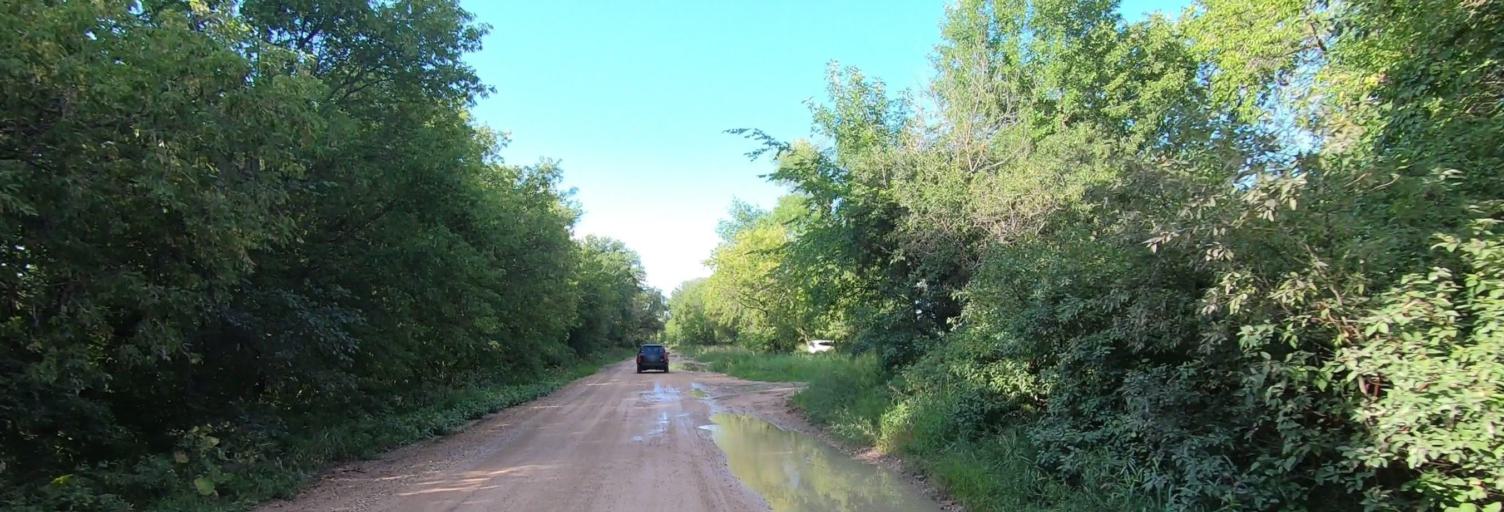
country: CA
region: Manitoba
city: Selkirk
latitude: 50.2651
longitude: -96.8495
